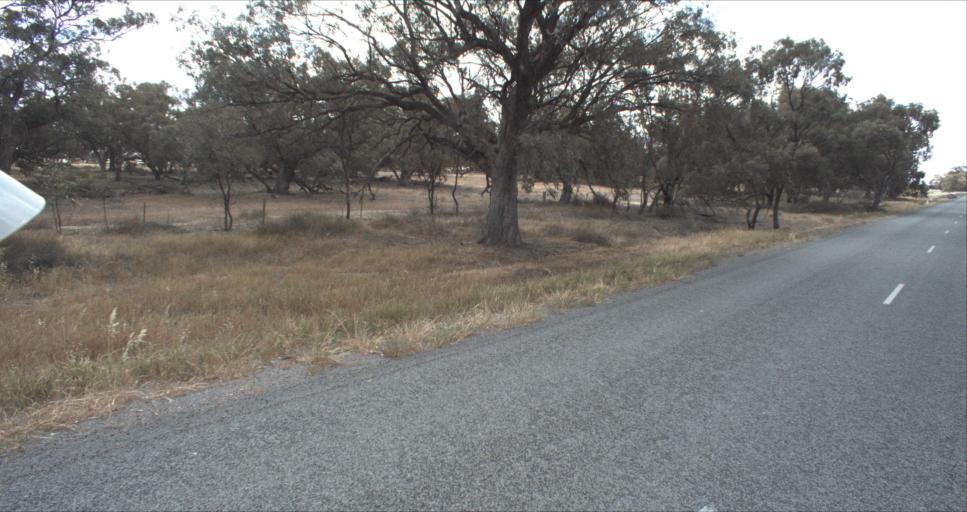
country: AU
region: New South Wales
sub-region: Leeton
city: Leeton
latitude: -34.6923
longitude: 146.3435
